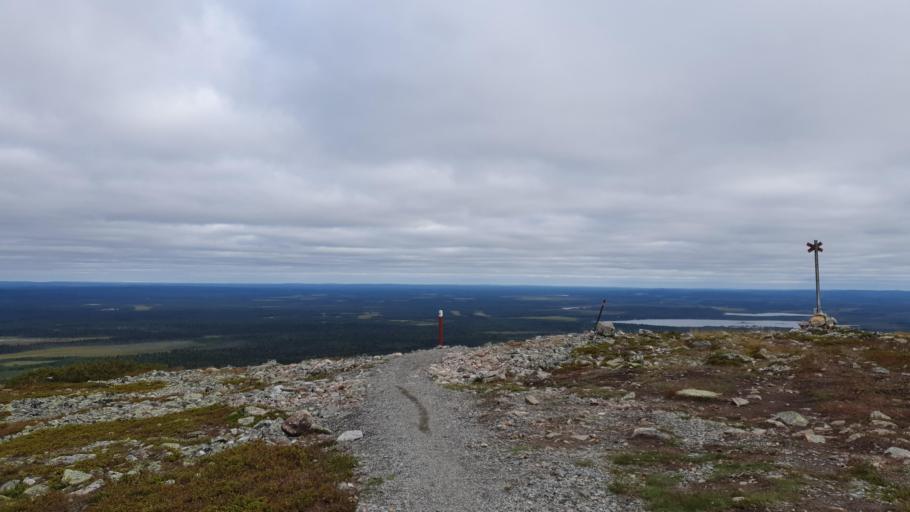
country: FI
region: Lapland
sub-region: Tunturi-Lappi
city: Kolari
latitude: 67.5683
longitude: 24.2449
